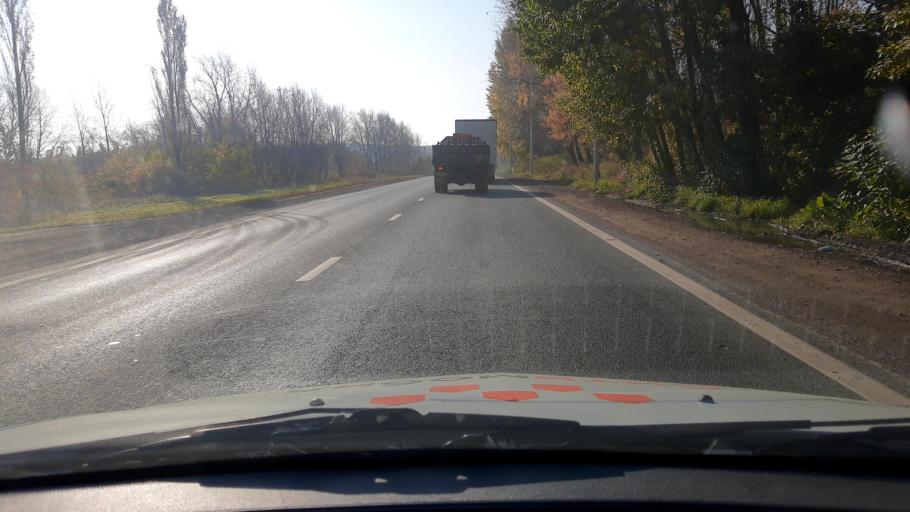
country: RU
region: Bashkortostan
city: Ufa
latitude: 54.8453
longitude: 56.1204
